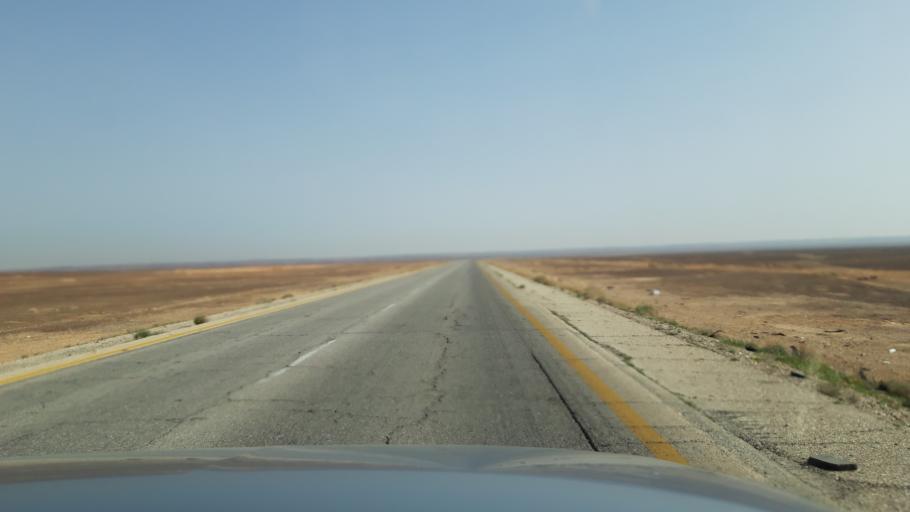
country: JO
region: Amman
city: Al Azraq ash Shamali
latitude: 31.8054
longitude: 36.5922
